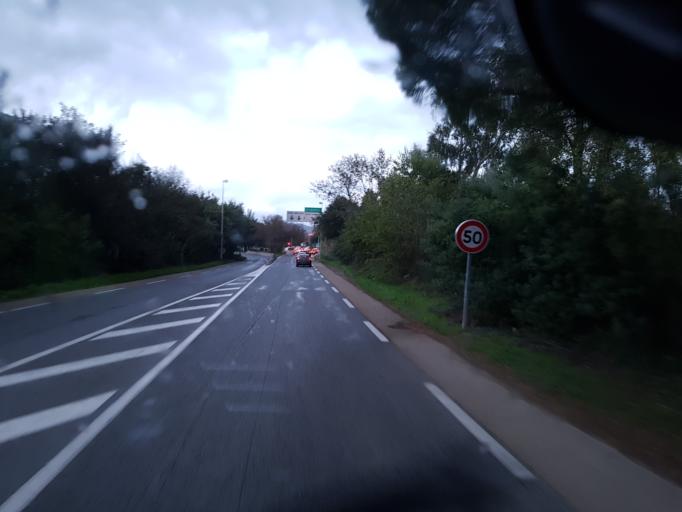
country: FR
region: Provence-Alpes-Cote d'Azur
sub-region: Departement du Var
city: Gassin
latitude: 43.2593
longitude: 6.5758
